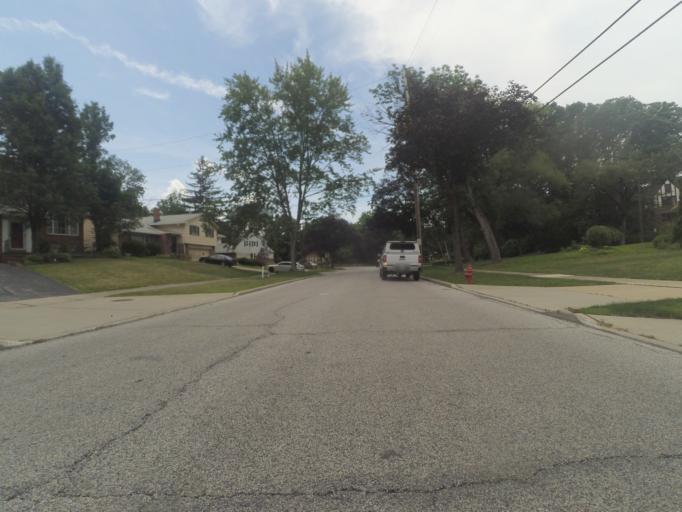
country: US
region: Ohio
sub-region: Cuyahoga County
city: University Heights
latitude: 41.4910
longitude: -81.5428
